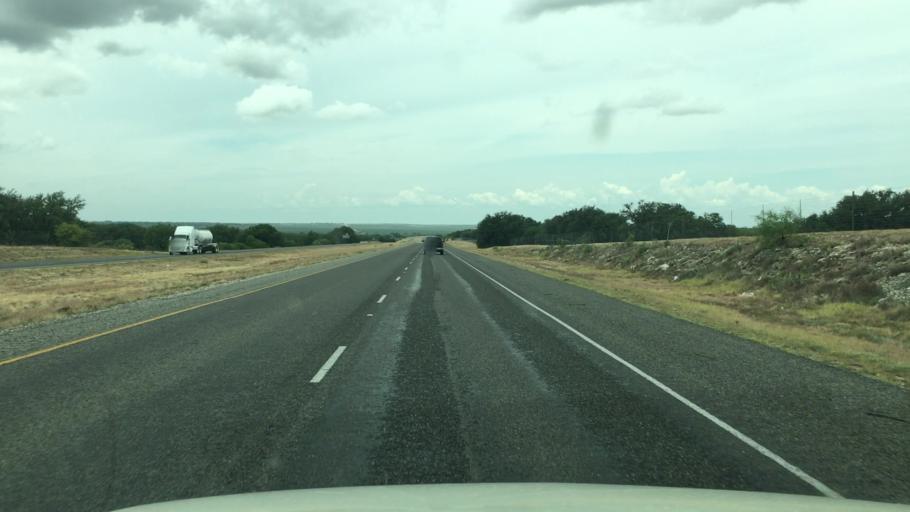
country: US
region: Texas
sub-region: Concho County
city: Eden
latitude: 31.2273
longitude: -99.9810
